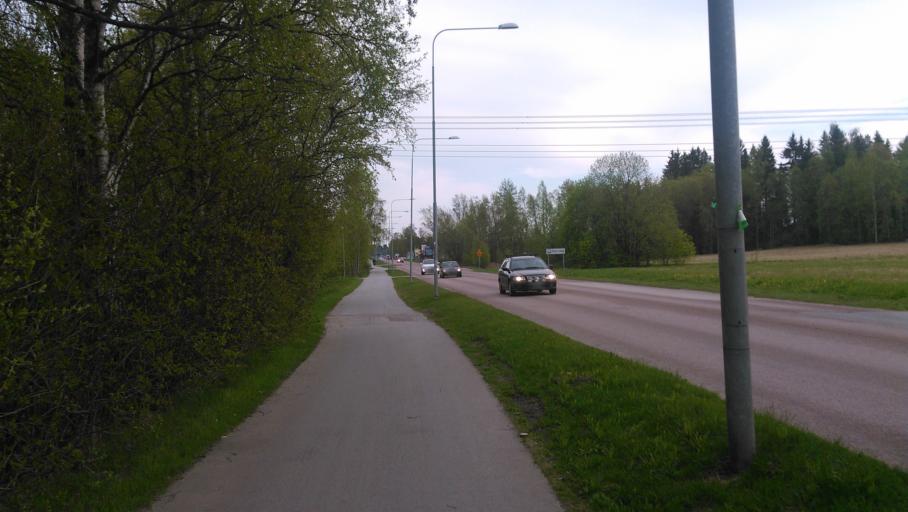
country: SE
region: Vaesterbotten
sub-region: Umea Kommun
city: Umea
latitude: 63.8092
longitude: 20.2706
